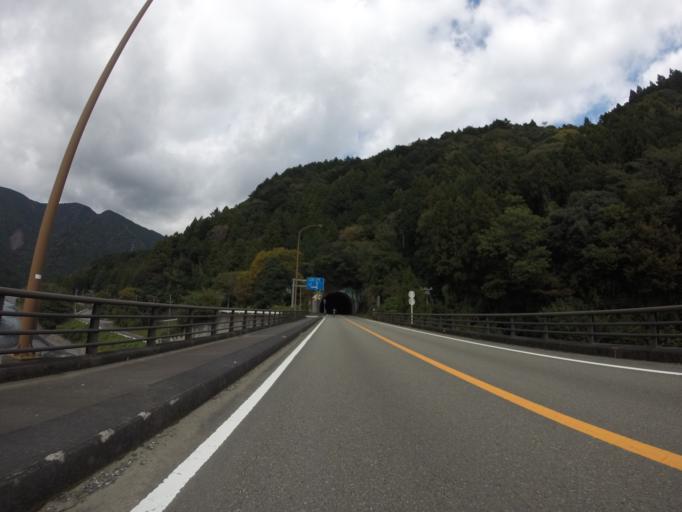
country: JP
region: Shizuoka
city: Fujieda
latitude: 35.0968
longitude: 138.1274
